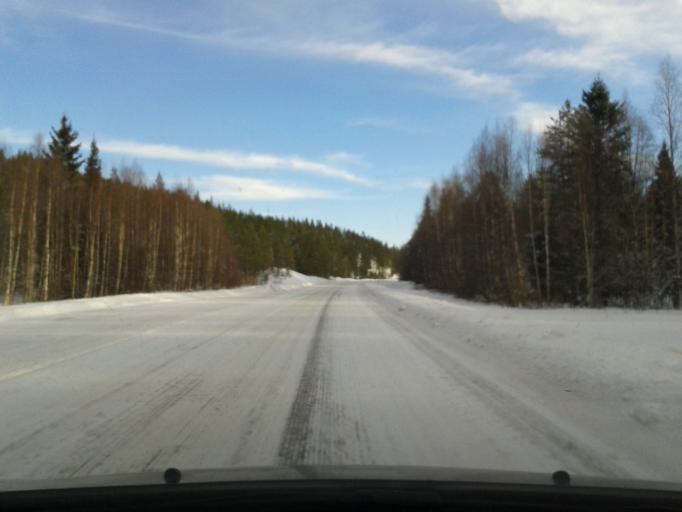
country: SE
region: Vaesterbotten
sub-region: Asele Kommun
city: Asele
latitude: 64.3207
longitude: 17.1126
